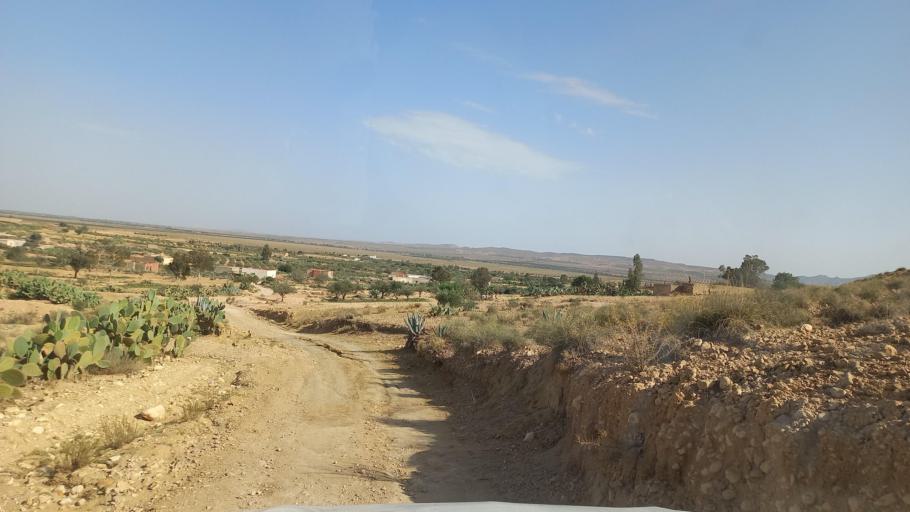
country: TN
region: Al Qasrayn
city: Kasserine
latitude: 35.2568
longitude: 8.9255
